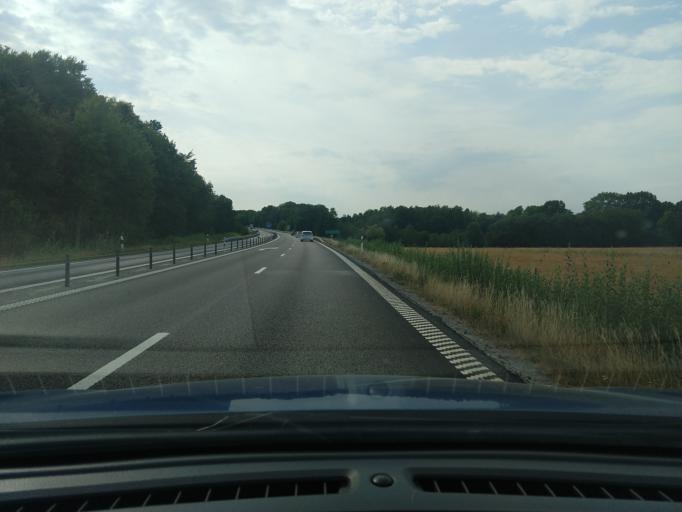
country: SE
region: Blekinge
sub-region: Karlskrona Kommun
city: Rodeby
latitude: 56.2020
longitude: 15.6710
